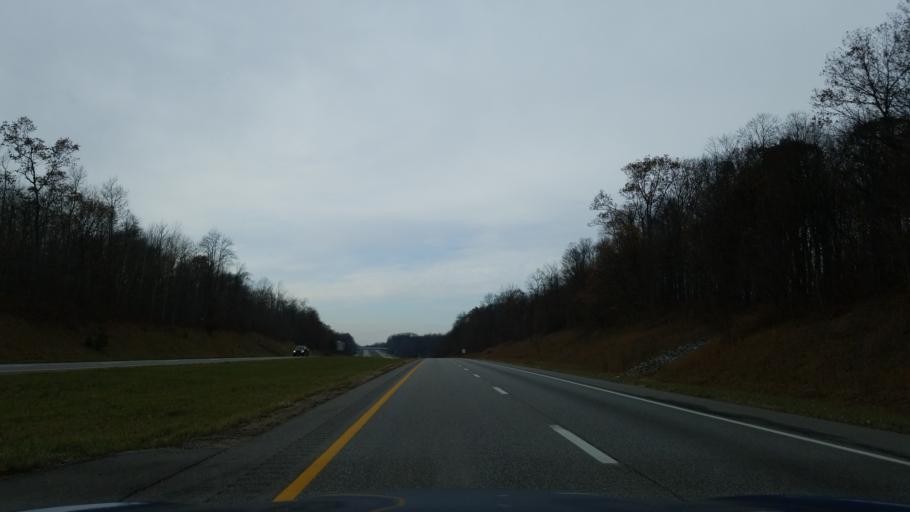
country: US
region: Ohio
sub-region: Portage County
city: Mantua
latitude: 41.3842
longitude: -81.2273
